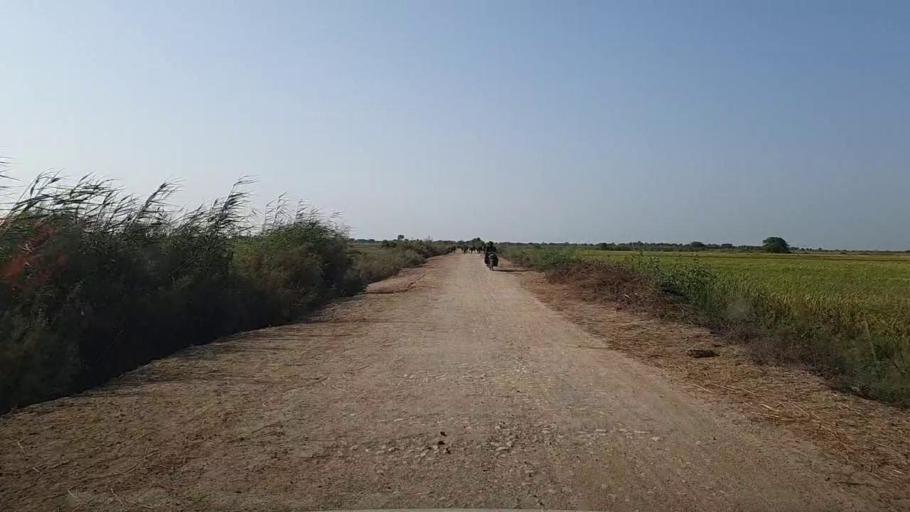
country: PK
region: Sindh
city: Kario
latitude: 24.8076
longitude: 68.5092
